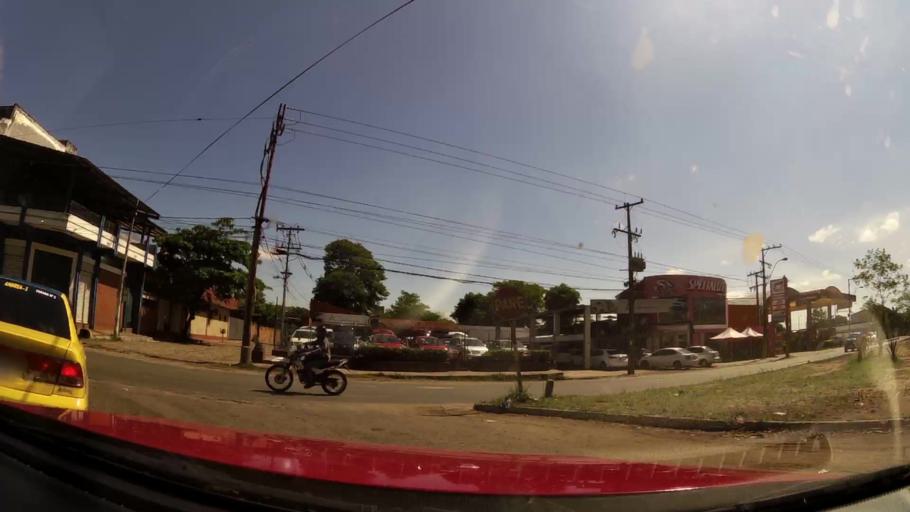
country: PY
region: Asuncion
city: Asuncion
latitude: -25.2561
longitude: -57.5709
